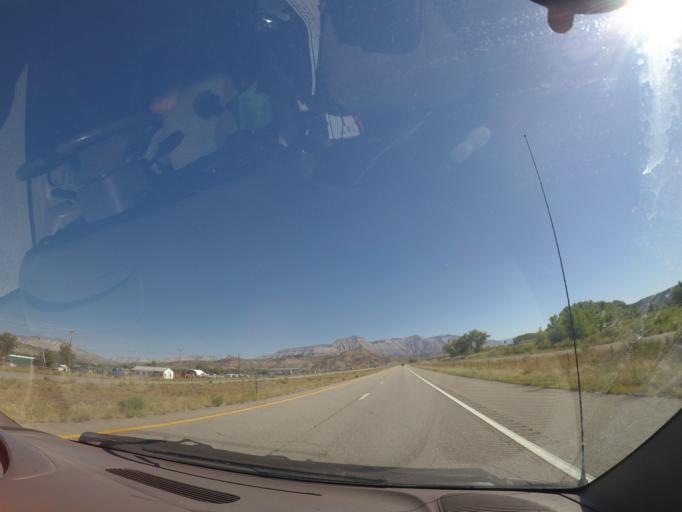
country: US
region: Colorado
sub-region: Garfield County
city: Parachute
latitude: 39.3173
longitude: -108.2117
